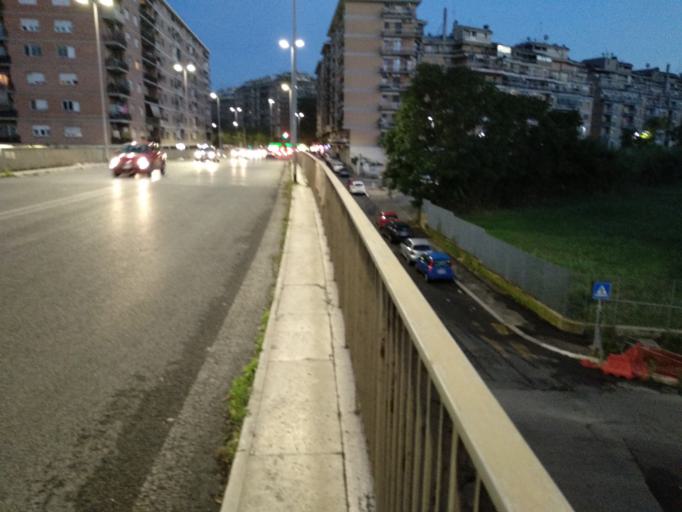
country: VA
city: Vatican City
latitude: 41.8666
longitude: 12.4634
